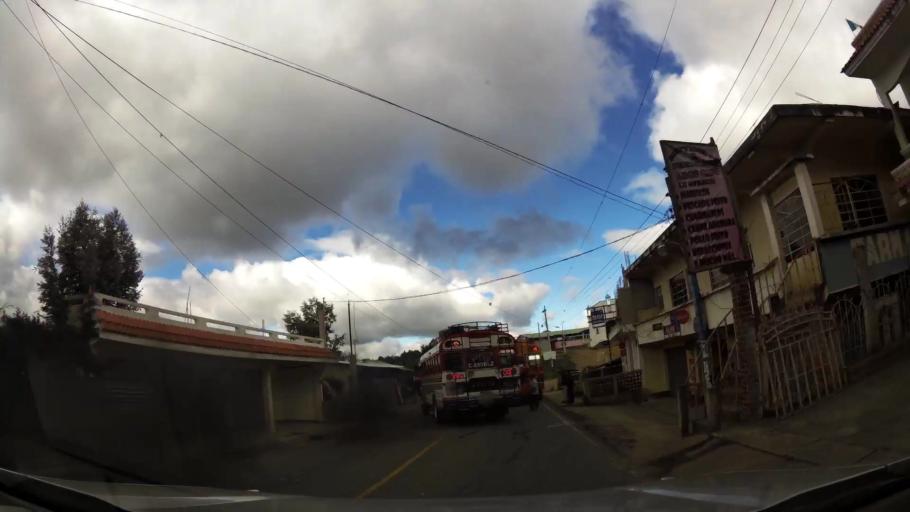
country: GT
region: Quiche
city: Chichicastenango
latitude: 14.9029
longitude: -91.1091
